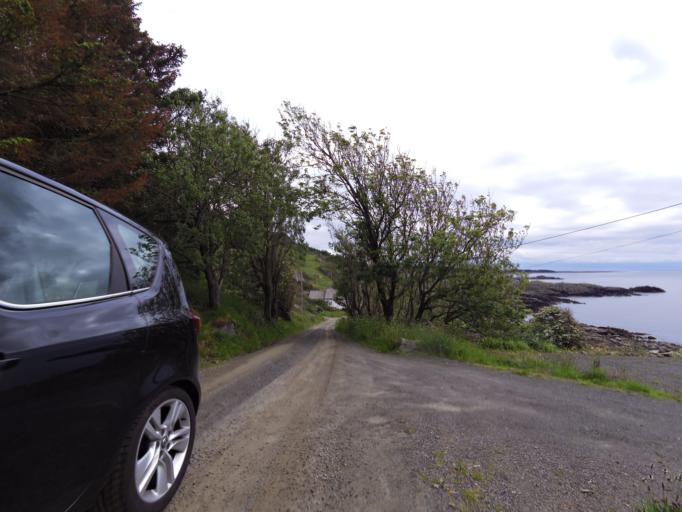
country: NO
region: Vest-Agder
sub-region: Farsund
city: Vestbygd
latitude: 58.1478
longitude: 6.6141
